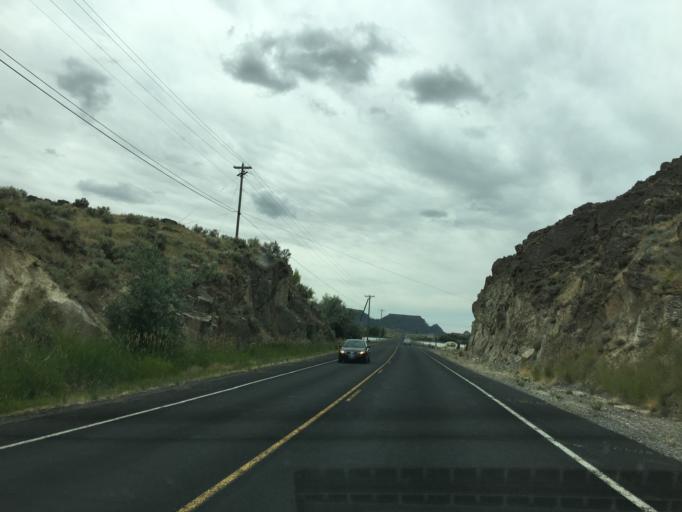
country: US
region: Washington
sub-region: Okanogan County
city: Coulee Dam
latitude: 47.9271
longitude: -119.0468
